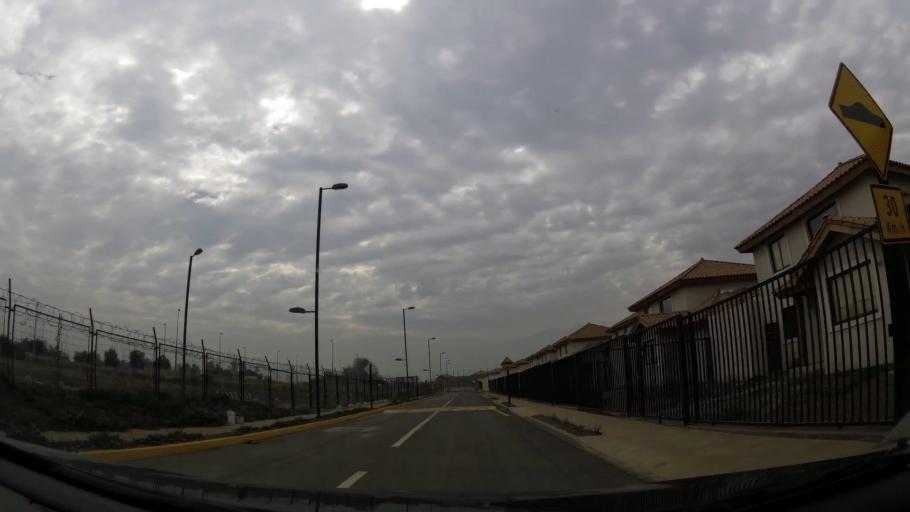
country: CL
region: Santiago Metropolitan
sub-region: Provincia de Chacabuco
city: Chicureo Abajo
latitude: -33.2205
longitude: -70.6766
